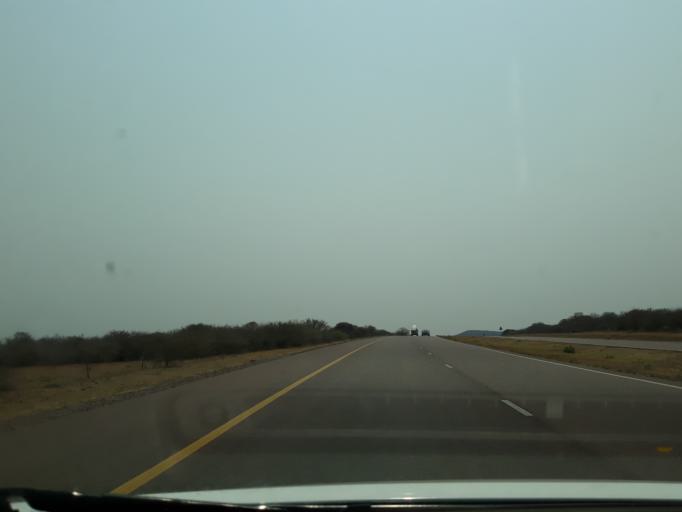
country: BW
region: Kgatleng
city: Bokaa
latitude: -24.4163
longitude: 26.0487
